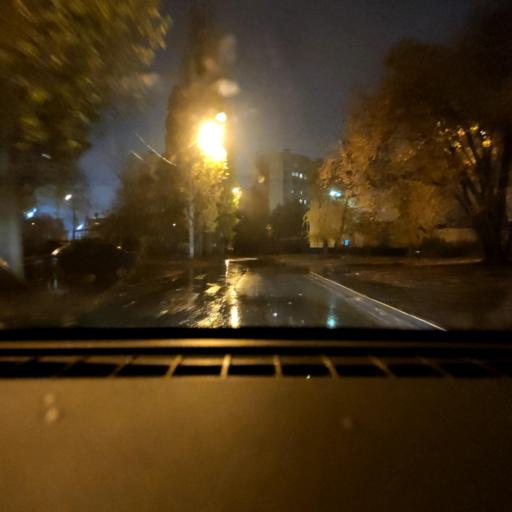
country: RU
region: Voronezj
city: Voronezh
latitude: 51.6430
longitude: 39.2696
